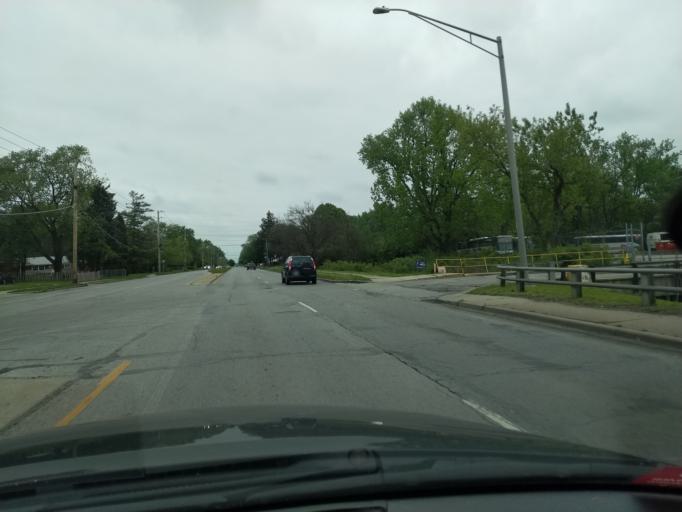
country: US
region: Indiana
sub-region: Marion County
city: Lawrence
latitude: 39.8266
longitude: -86.0648
